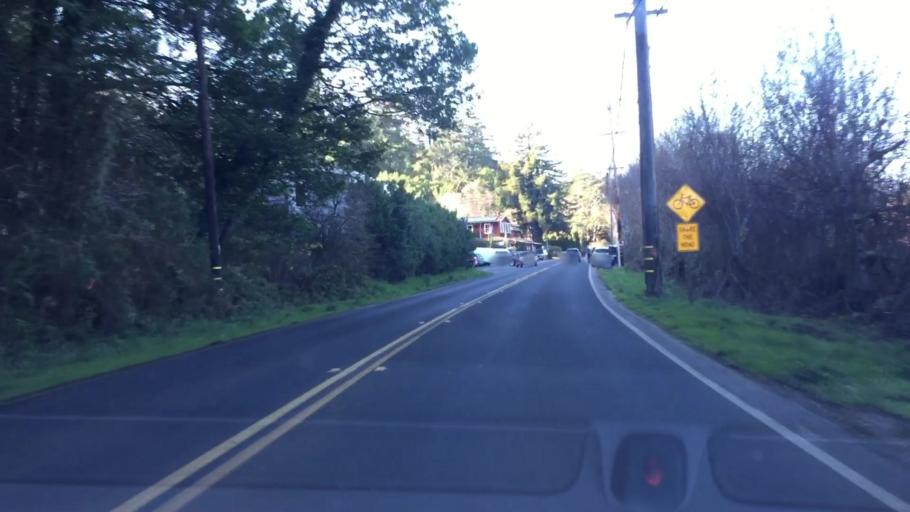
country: US
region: California
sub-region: Marin County
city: Inverness
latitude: 38.0688
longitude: -122.8238
